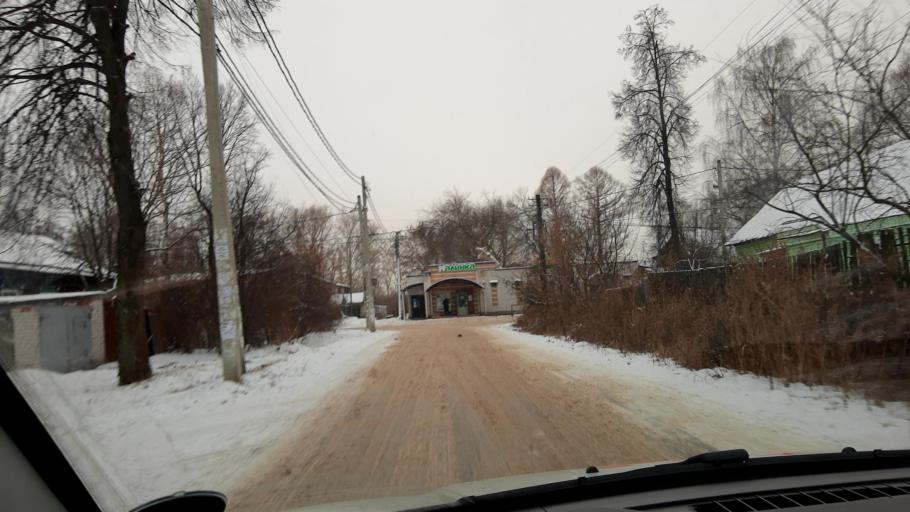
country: RU
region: Nizjnij Novgorod
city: Burevestnik
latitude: 56.1992
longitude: 43.7704
